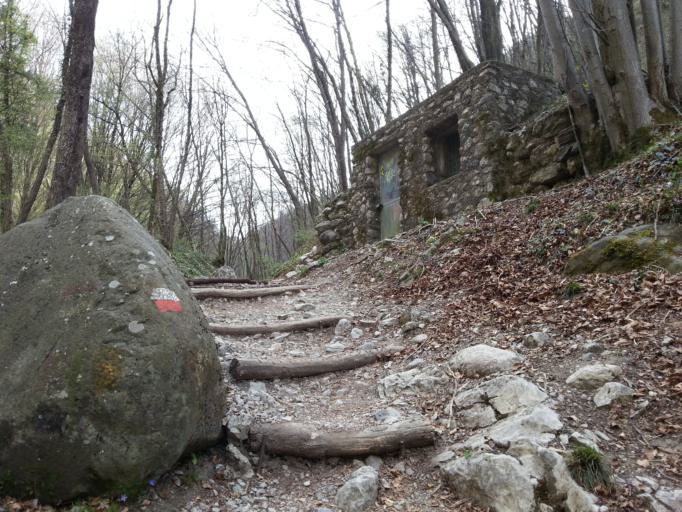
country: IT
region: Lombardy
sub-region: Provincia di Como
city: Osigo
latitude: 45.8522
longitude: 9.3007
